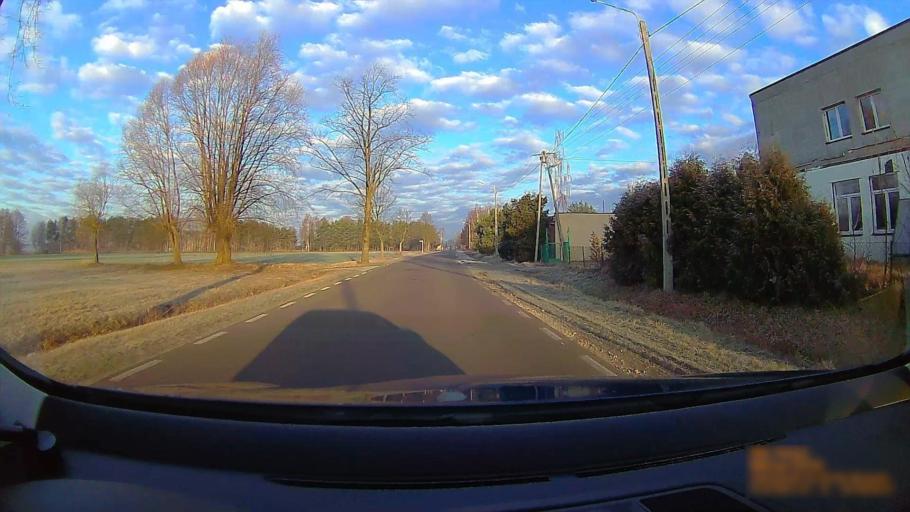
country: PL
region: Greater Poland Voivodeship
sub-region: Powiat koninski
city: Rzgow Pierwszy
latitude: 52.1010
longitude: 18.0984
